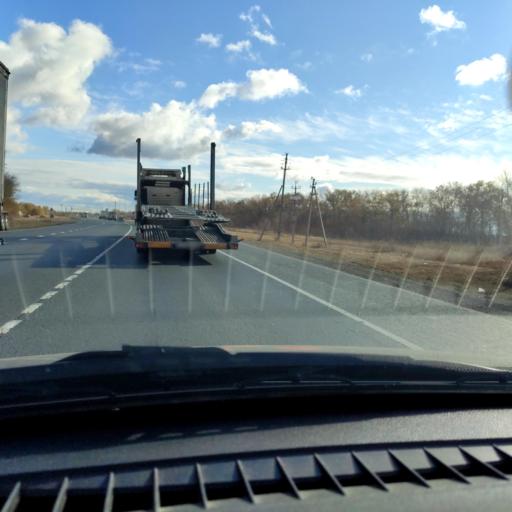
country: RU
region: Samara
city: Varlamovo
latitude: 53.1923
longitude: 48.3380
